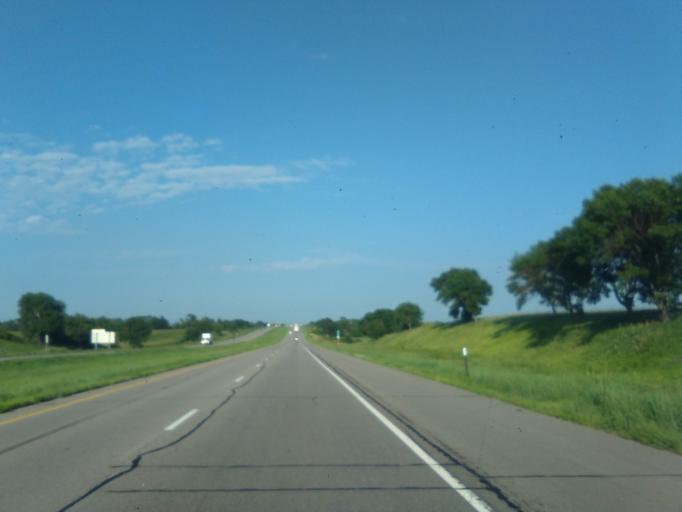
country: US
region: Nebraska
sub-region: Saline County
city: Friend
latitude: 40.8222
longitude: -97.2692
